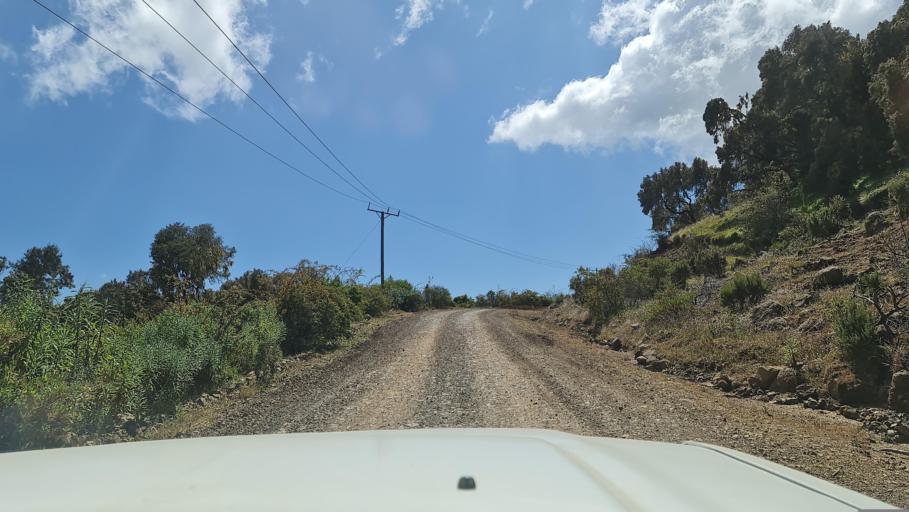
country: ET
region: Amhara
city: Debark'
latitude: 13.2225
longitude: 38.0150
